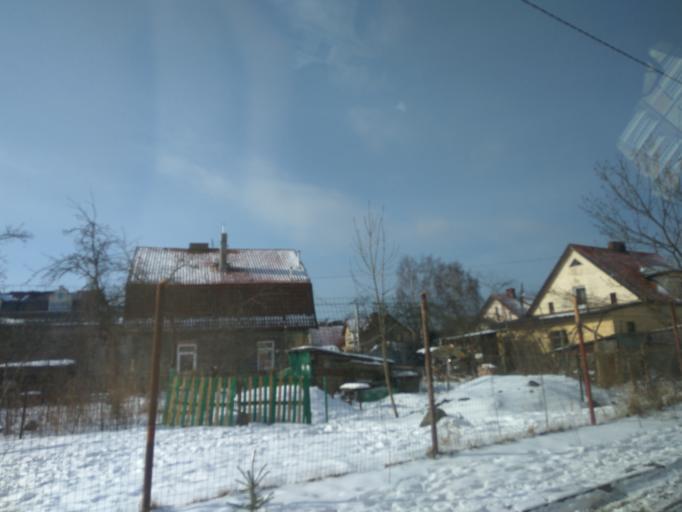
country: RU
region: Kaliningrad
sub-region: Zelenogradskiy Rayon
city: Zelenogradsk
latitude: 54.9576
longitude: 20.4867
